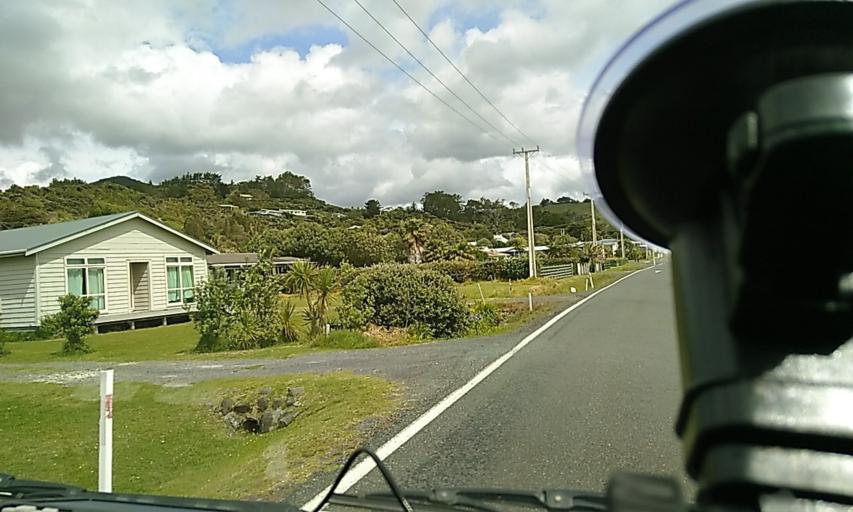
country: NZ
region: Northland
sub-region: Far North District
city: Ahipara
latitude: -35.5207
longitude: 173.3883
